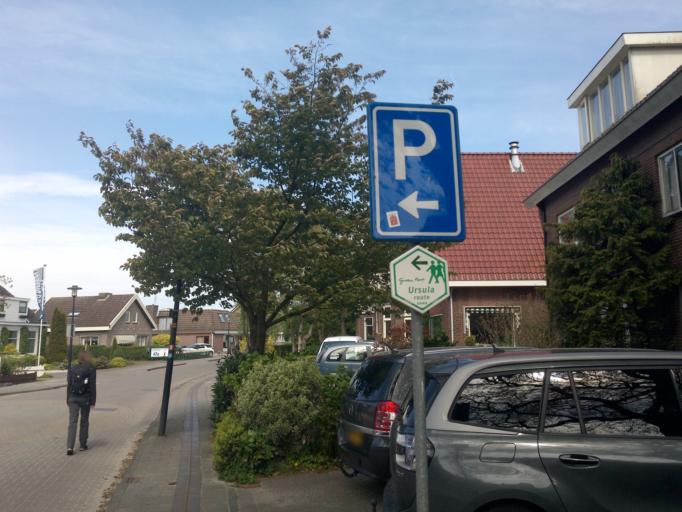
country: NL
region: South Holland
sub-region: Gemeente Nieuwkoop
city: Nieuwkoop
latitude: 52.1998
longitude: 4.7592
